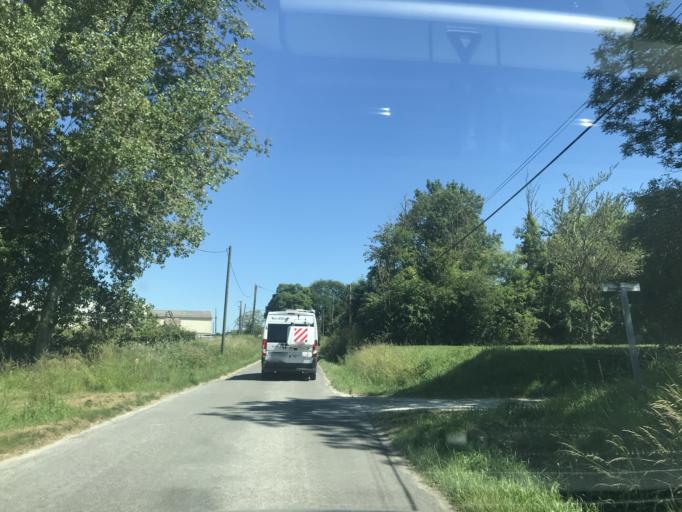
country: FR
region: Poitou-Charentes
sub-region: Departement de la Charente-Maritime
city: Mortagne-sur-Gironde
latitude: 45.4254
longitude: -0.7269
